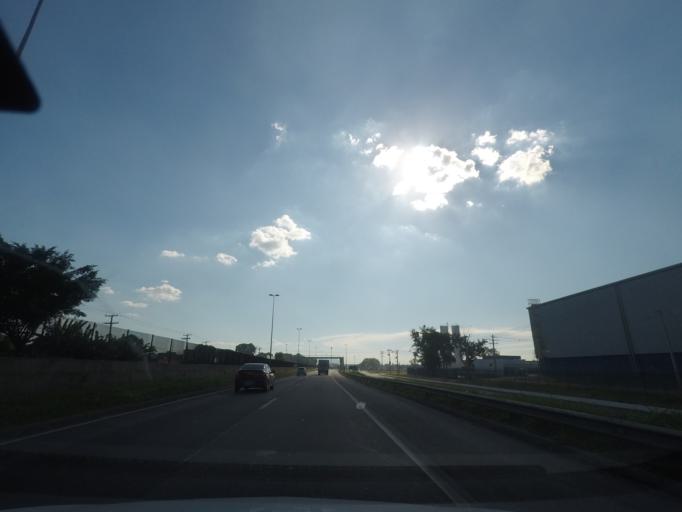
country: BR
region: Rio de Janeiro
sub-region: Duque De Caxias
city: Duque de Caxias
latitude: -22.6647
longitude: -43.2595
